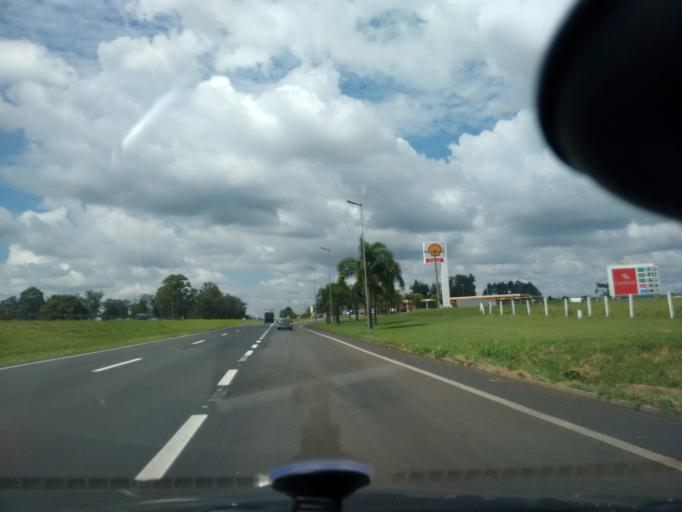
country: BR
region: Sao Paulo
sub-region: Sao Carlos
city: Sao Carlos
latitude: -22.0895
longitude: -47.8335
